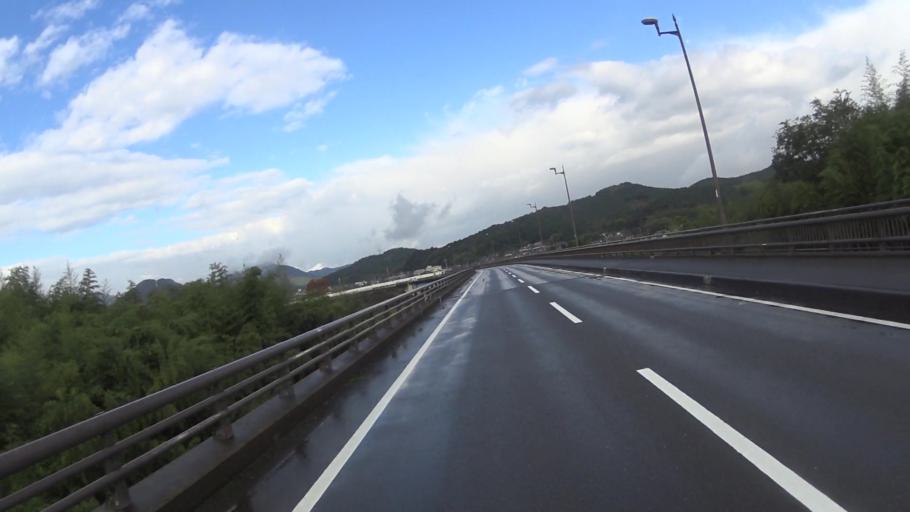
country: JP
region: Kyoto
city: Ayabe
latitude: 35.3069
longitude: 135.2308
